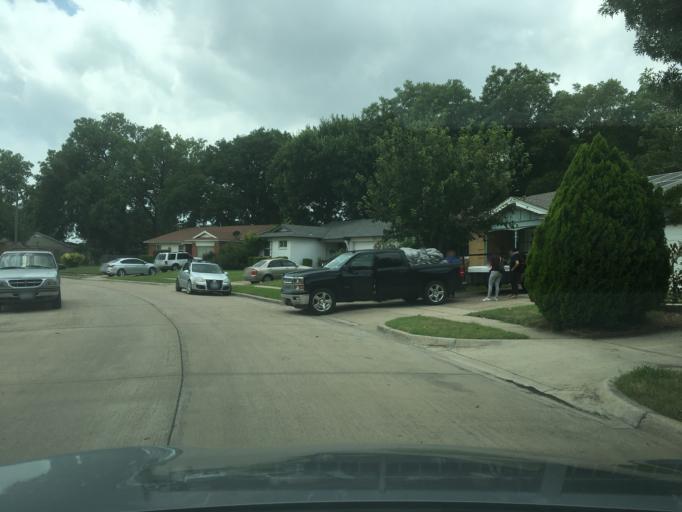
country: US
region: Texas
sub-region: Dallas County
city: Garland
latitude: 32.9190
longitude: -96.6774
